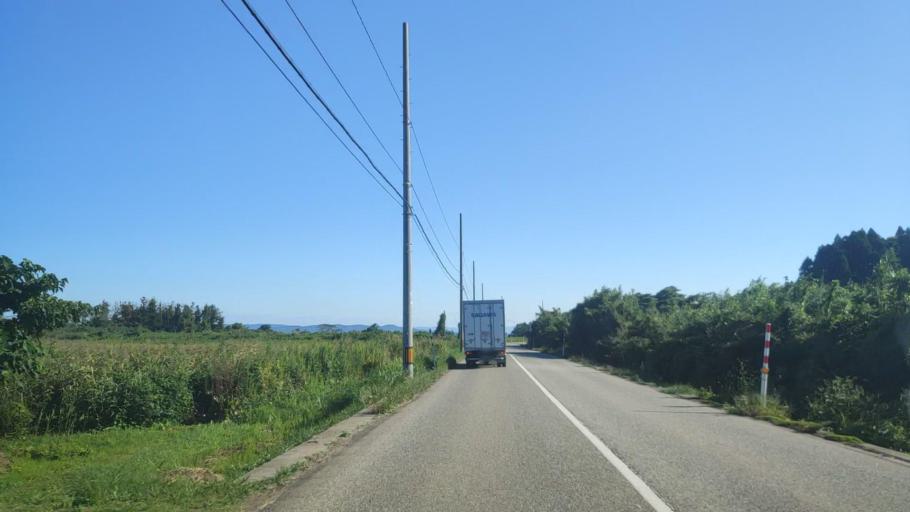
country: JP
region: Ishikawa
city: Nanao
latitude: 37.1964
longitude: 136.9104
